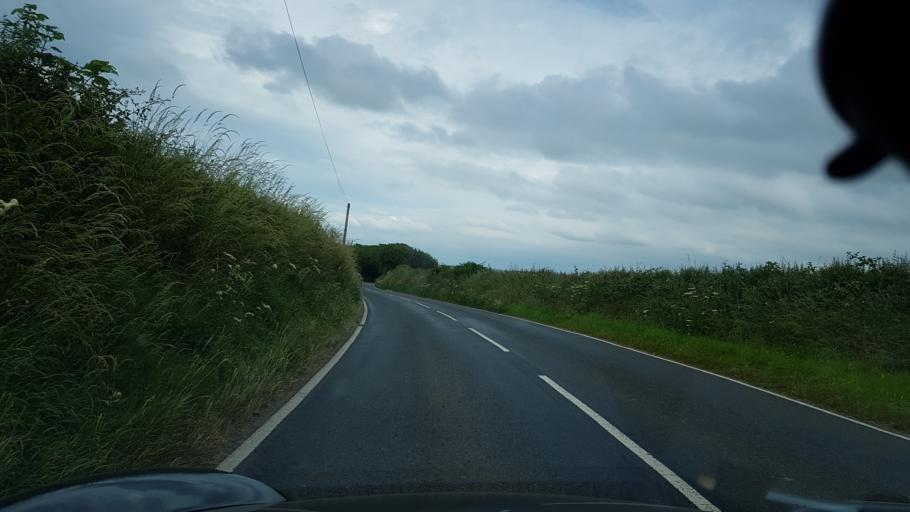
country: GB
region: Wales
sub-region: Pembrokeshire
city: Herbrandston
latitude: 51.7725
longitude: -5.0558
